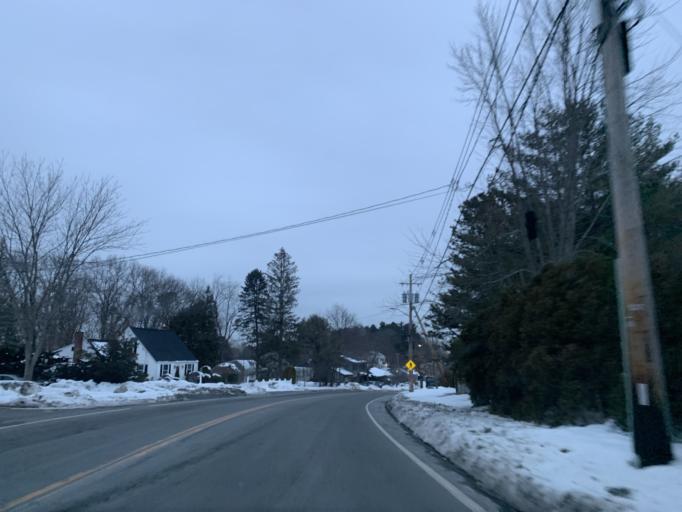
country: US
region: Massachusetts
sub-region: Norfolk County
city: Stoughton
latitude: 42.1420
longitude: -71.1170
